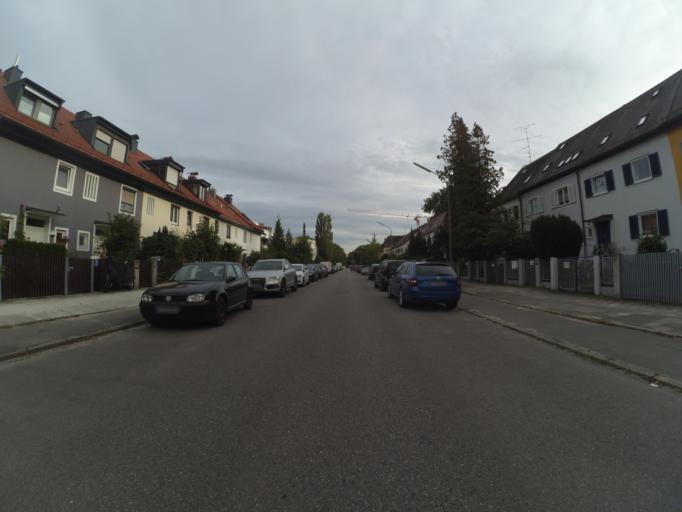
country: DE
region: Bavaria
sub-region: Upper Bavaria
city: Munich
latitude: 48.1652
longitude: 11.5190
